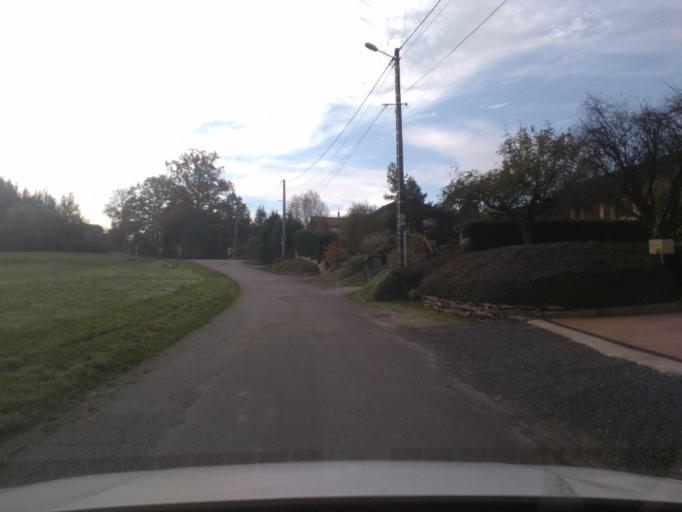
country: FR
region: Lorraine
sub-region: Departement des Vosges
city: Saint-Michel-sur-Meurthe
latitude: 48.3452
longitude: 6.8976
